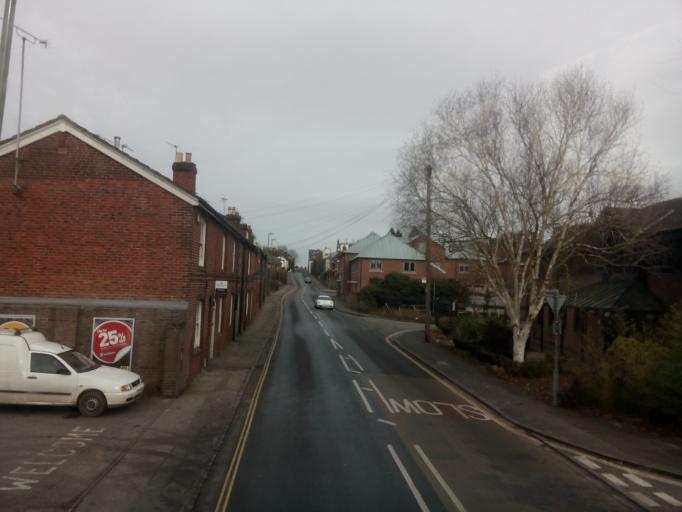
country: GB
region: England
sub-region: Hampshire
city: Winchester
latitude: 51.0549
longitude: -1.3059
